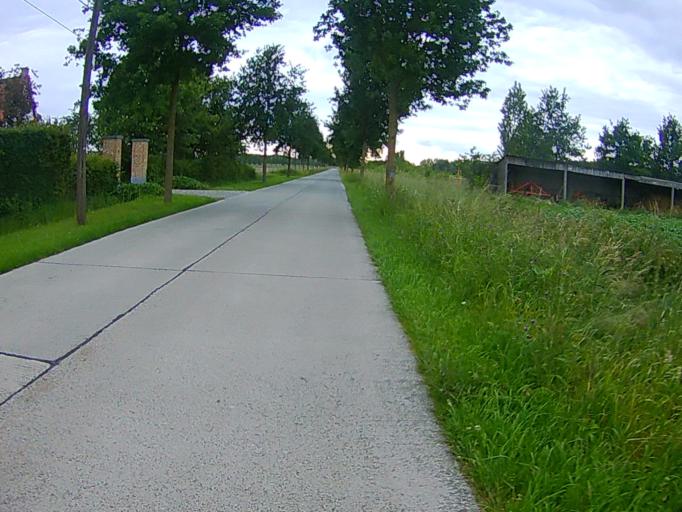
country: BE
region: Flanders
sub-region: Provincie Antwerpen
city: Lier
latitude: 51.0921
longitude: 4.5908
